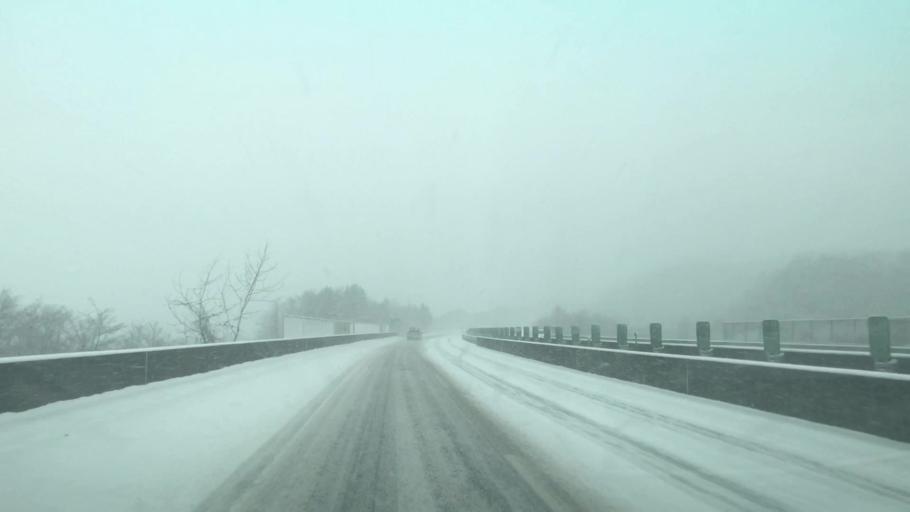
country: JP
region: Hokkaido
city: Shiraoi
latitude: 42.5016
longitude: 141.2652
